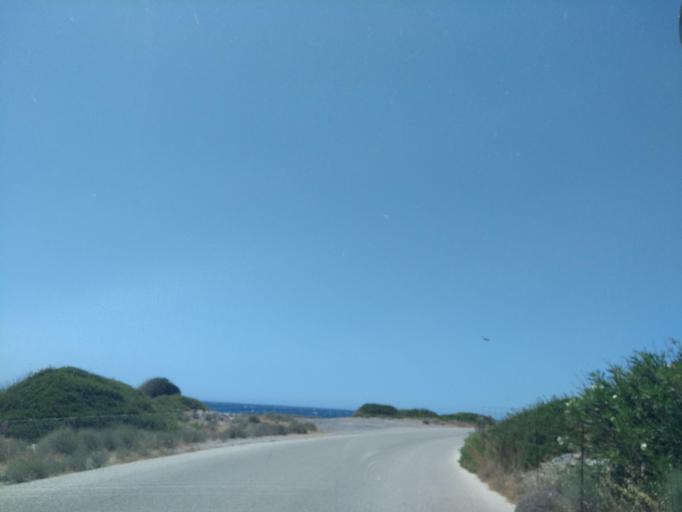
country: GR
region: Crete
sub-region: Nomos Chanias
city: Vryses
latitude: 35.3538
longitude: 23.5341
